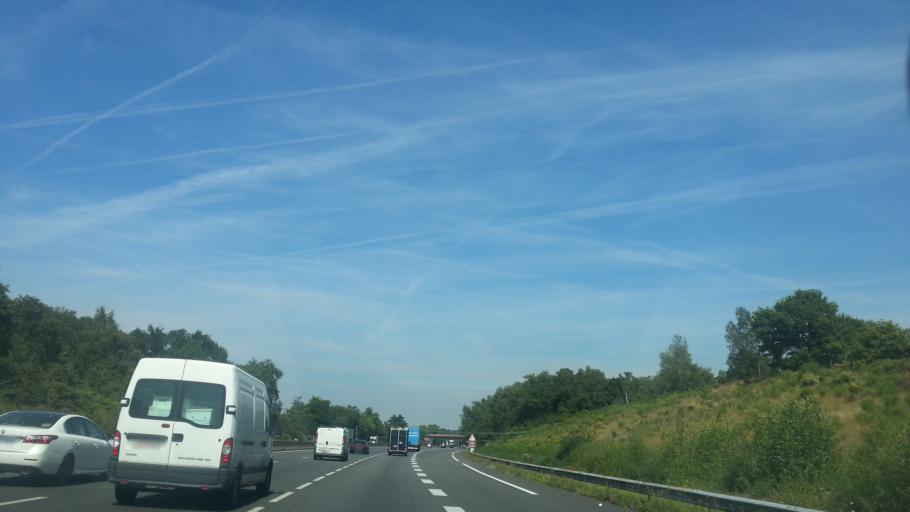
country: FR
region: Picardie
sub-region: Departement de l'Oise
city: La Chapelle-en-Serval
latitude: 49.1293
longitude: 2.5589
